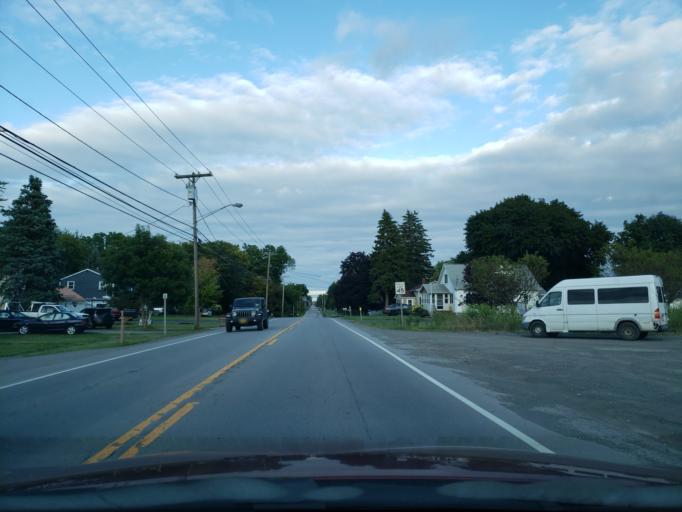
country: US
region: New York
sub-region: Monroe County
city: Greece
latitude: 43.2536
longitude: -77.7321
